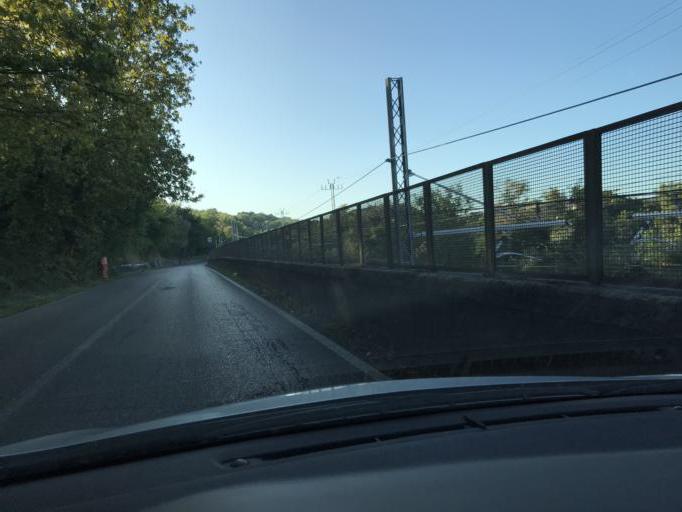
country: IT
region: Latium
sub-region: Provincia di Viterbo
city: Orte Scalo
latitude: 42.4463
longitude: 12.3952
